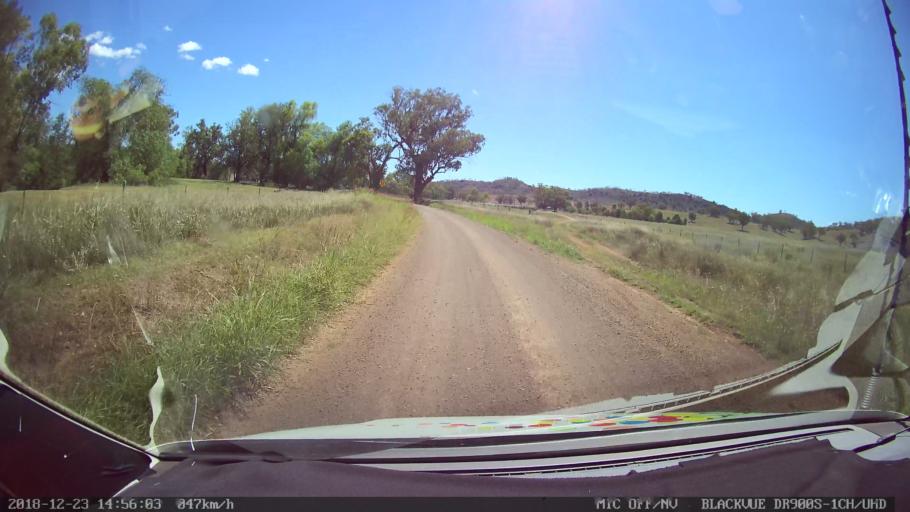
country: AU
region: New South Wales
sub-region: Tamworth Municipality
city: Manilla
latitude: -30.7022
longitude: 150.8313
